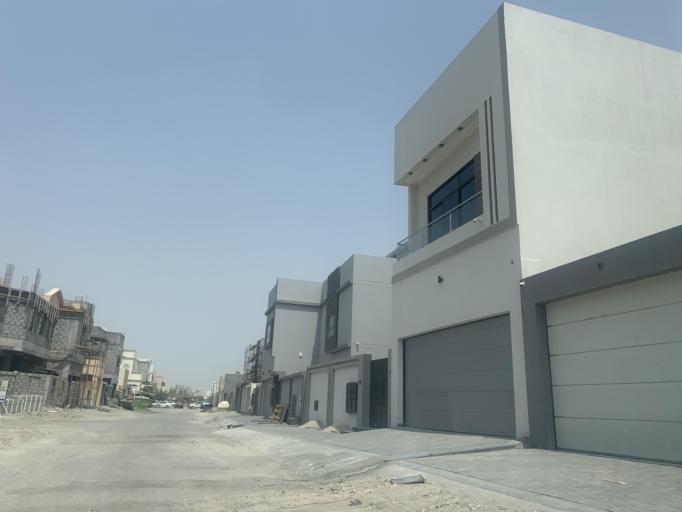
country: BH
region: Central Governorate
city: Madinat Hamad
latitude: 26.1300
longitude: 50.4672
